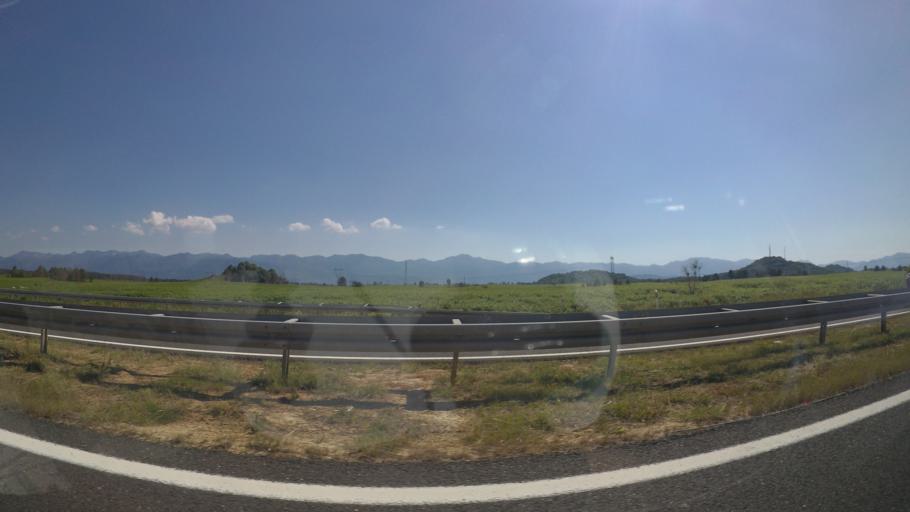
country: HR
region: Licko-Senjska
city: Gospic
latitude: 44.5220
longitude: 15.4628
